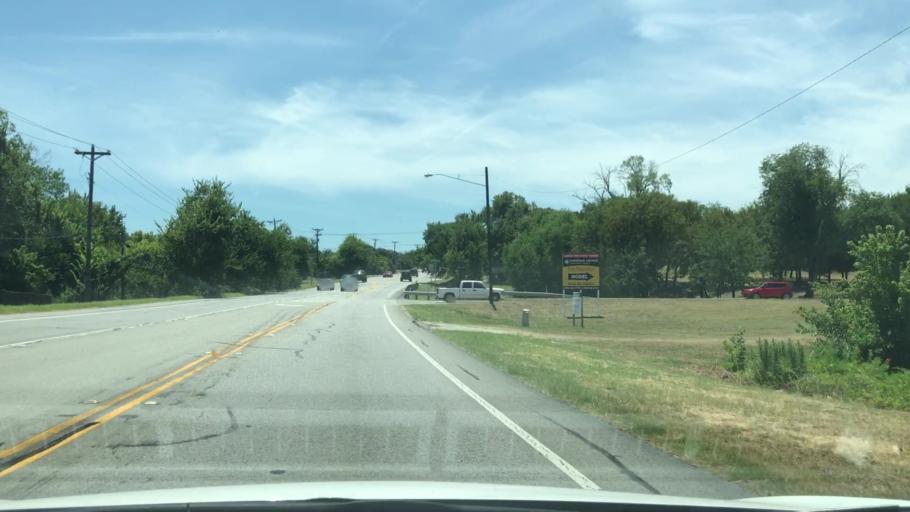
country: US
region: Texas
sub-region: Rockwall County
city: Rockwall
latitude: 32.9414
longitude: -96.4602
